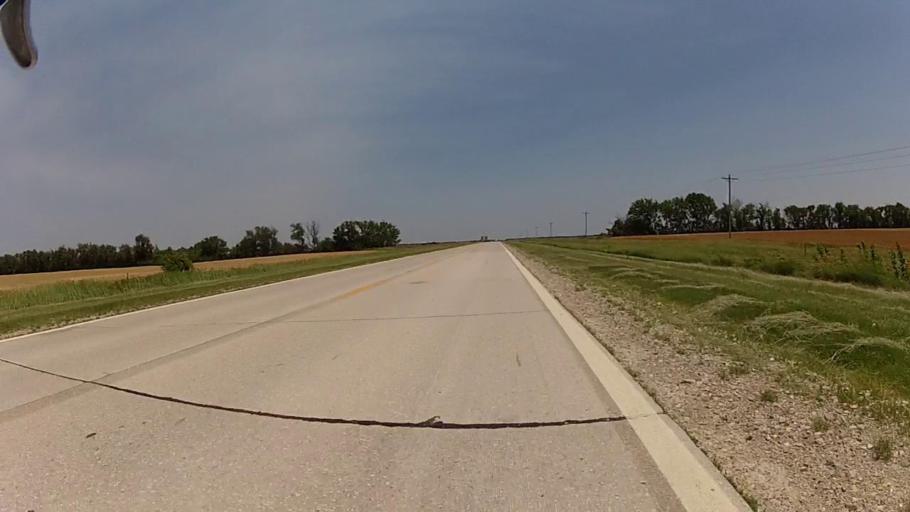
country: US
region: Kansas
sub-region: Cowley County
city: Arkansas City
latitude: 37.0575
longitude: -97.2664
